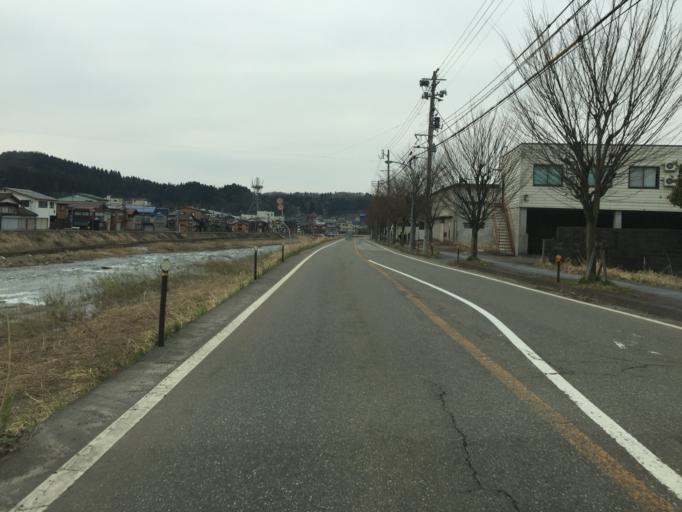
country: JP
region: Niigata
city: Tochio-honcho
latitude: 37.4755
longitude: 138.9997
